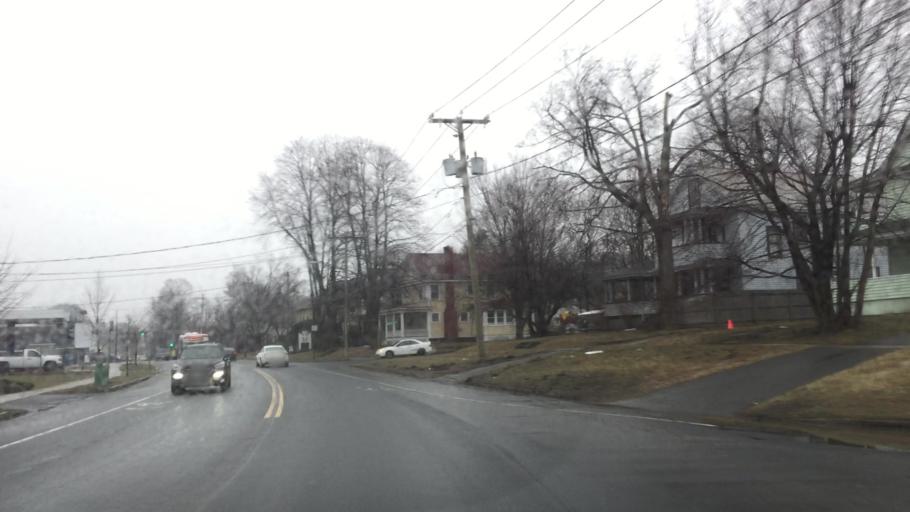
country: US
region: Massachusetts
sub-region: Berkshire County
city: Pittsfield
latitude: 42.4447
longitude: -73.2435
